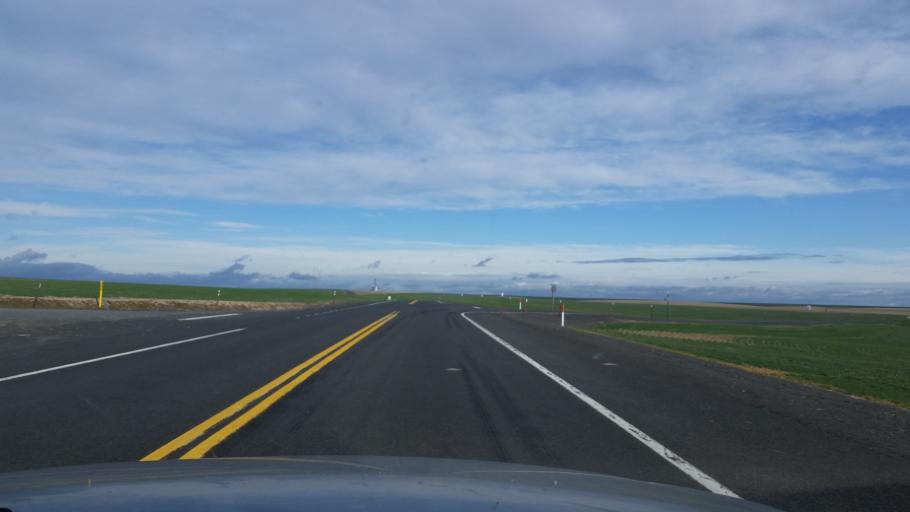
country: US
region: Washington
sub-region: Adams County
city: Ritzville
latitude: 47.4063
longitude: -118.3824
